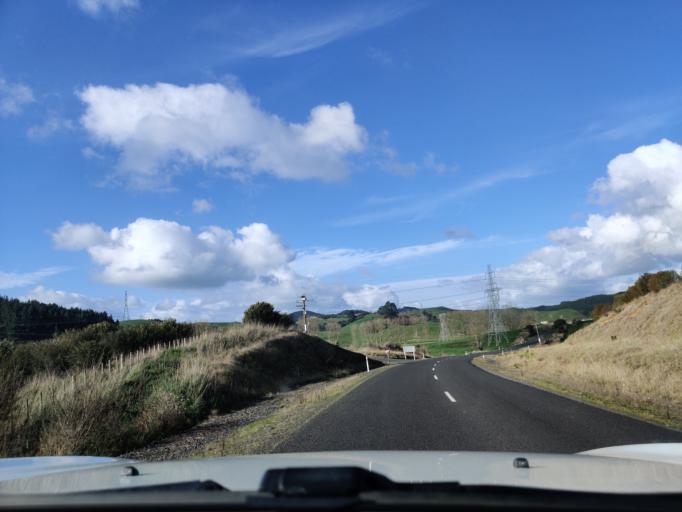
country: NZ
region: Waikato
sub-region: Waikato District
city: Te Kauwhata
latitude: -37.2829
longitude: 175.2061
